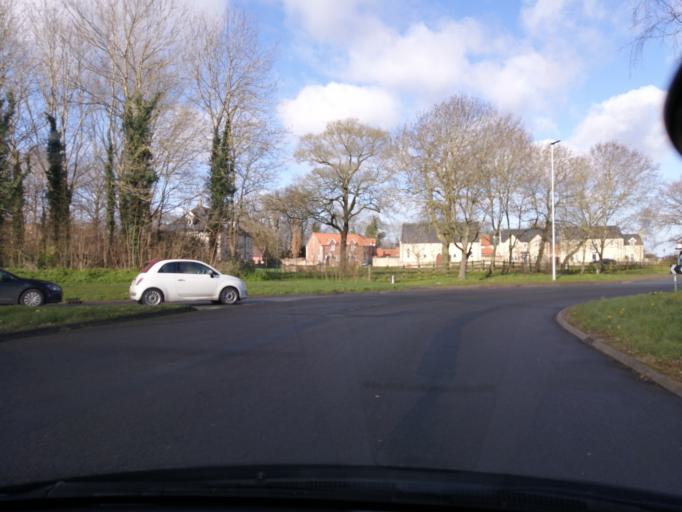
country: GB
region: England
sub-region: Peterborough
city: Marholm
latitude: 52.5878
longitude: -0.2859
